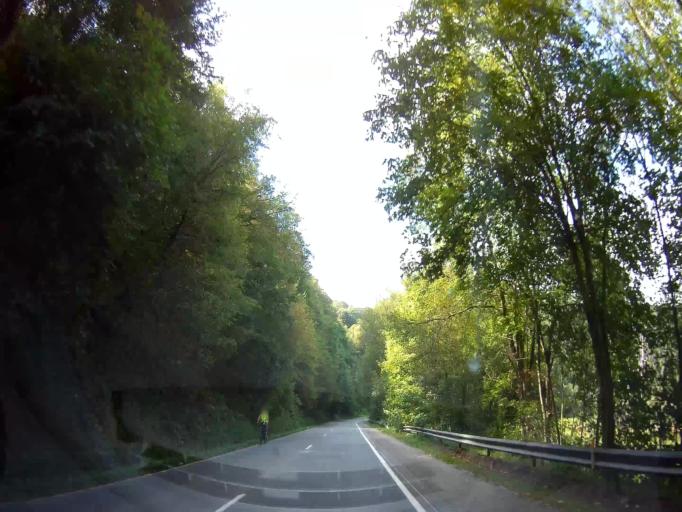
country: BE
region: Wallonia
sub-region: Province du Luxembourg
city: Rendeux
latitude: 50.2074
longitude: 5.5269
